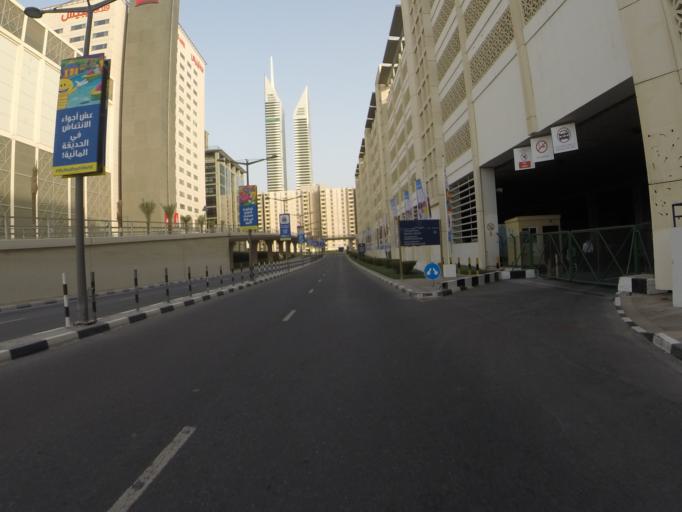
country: AE
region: Ash Shariqah
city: Sharjah
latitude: 25.2212
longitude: 55.2873
